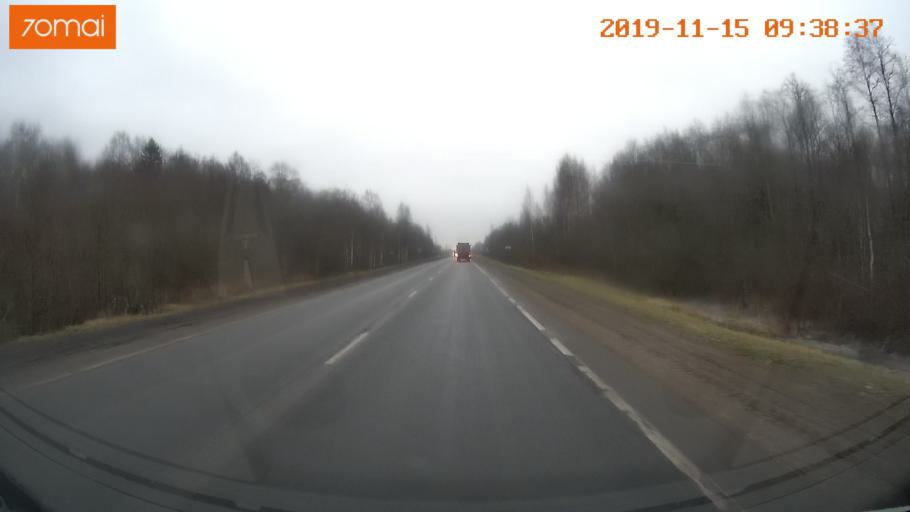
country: RU
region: Vologda
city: Sheksna
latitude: 59.2302
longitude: 38.4591
